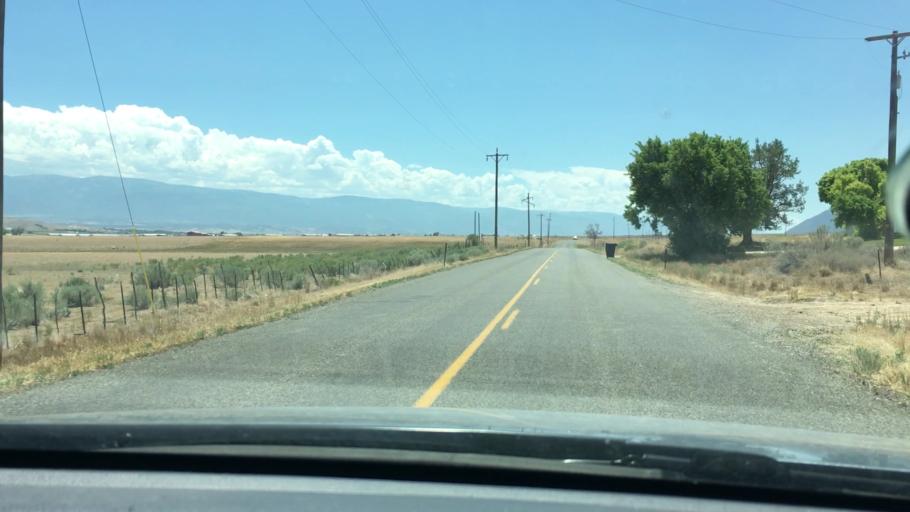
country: US
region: Utah
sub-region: Sanpete County
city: Fountain Green
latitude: 39.5862
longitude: -111.6415
